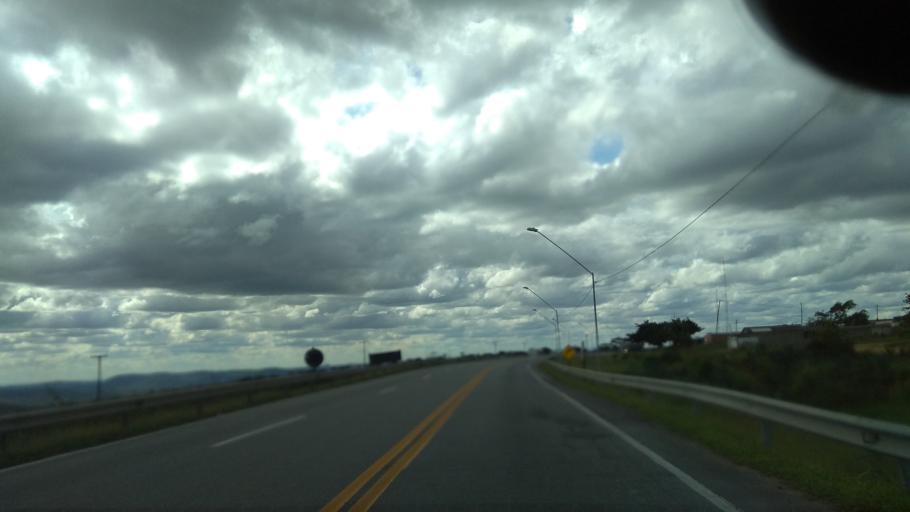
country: BR
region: Bahia
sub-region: Santa Ines
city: Santa Ines
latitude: -13.0689
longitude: -39.9608
